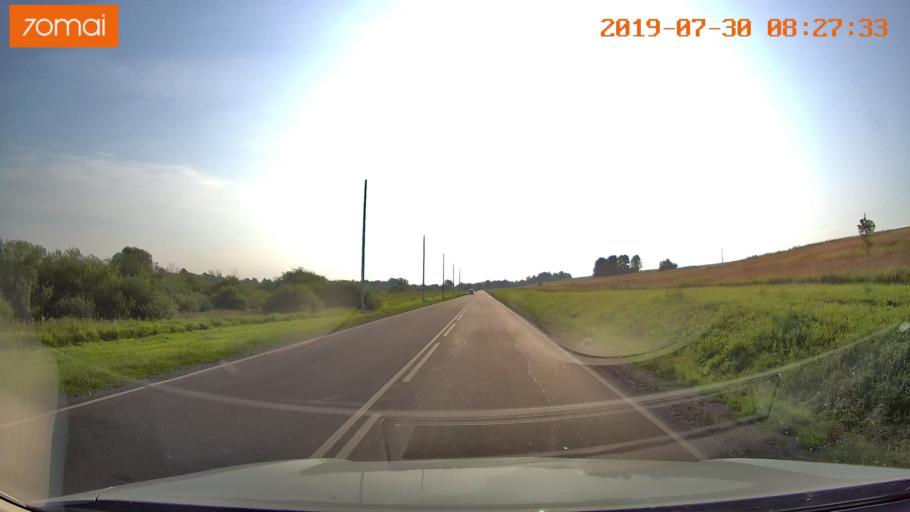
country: RU
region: Kaliningrad
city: Chernyakhovsk
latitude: 54.6278
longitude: 21.6275
